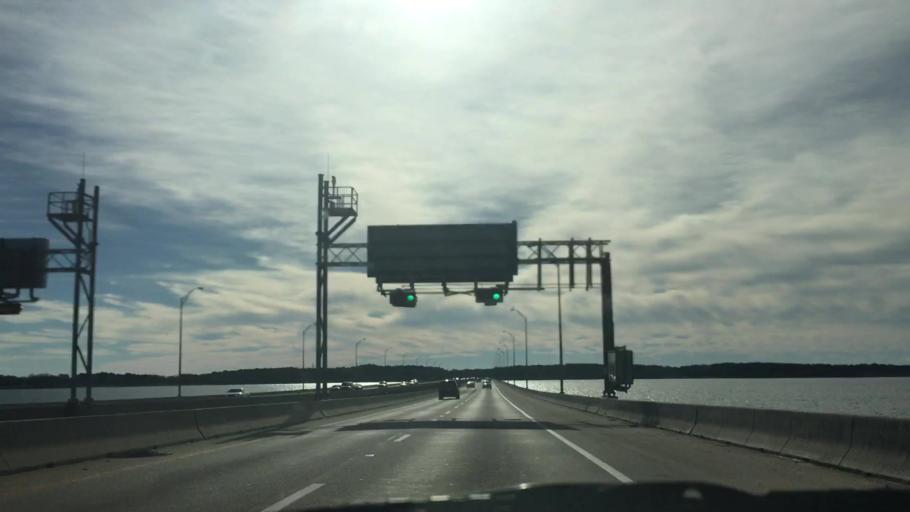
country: US
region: Virginia
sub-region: City of Newport News
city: Newport News
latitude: 36.9156
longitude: -76.4141
